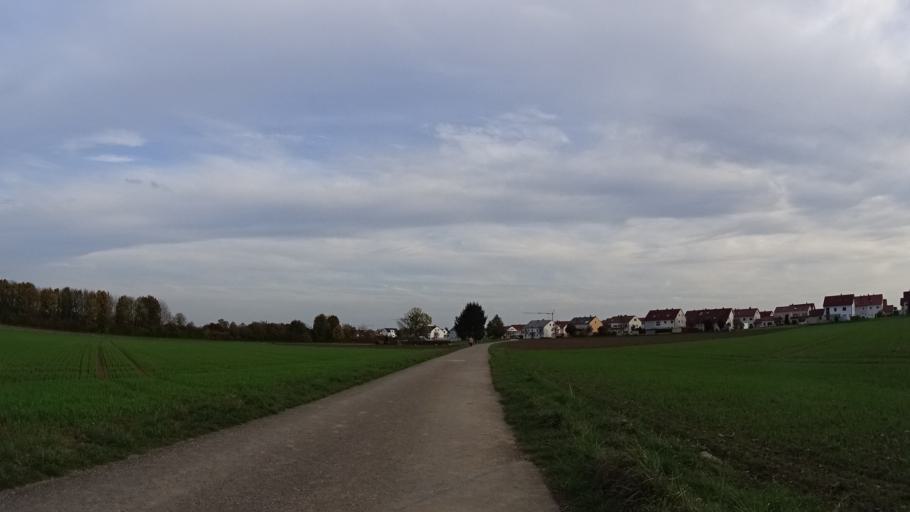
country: DE
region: Bavaria
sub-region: Upper Bavaria
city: Gaimersheim
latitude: 48.8178
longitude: 11.3633
